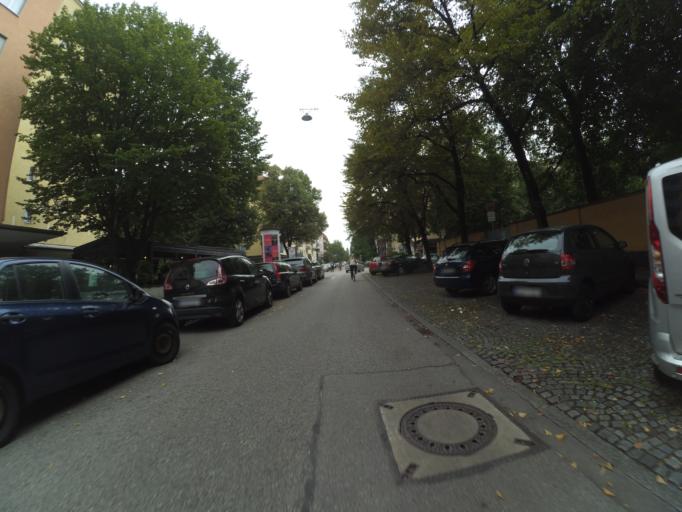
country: DE
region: Bavaria
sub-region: Upper Bavaria
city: Munich
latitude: 48.1600
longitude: 11.5652
